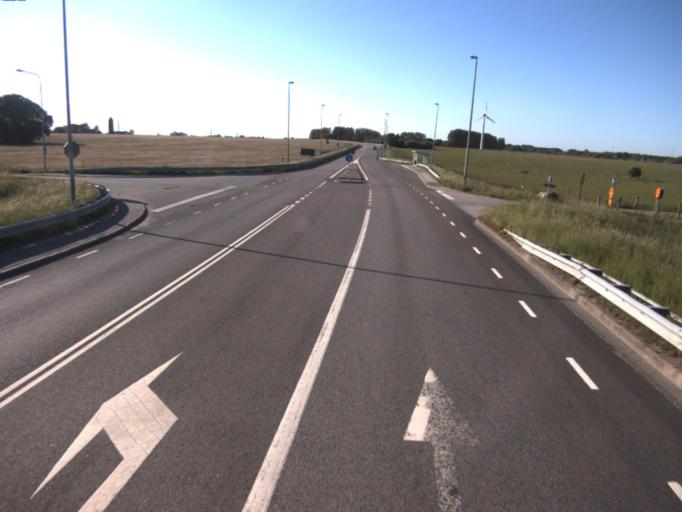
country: SE
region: Skane
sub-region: Helsingborg
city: Rydeback
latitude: 55.9887
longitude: 12.7651
